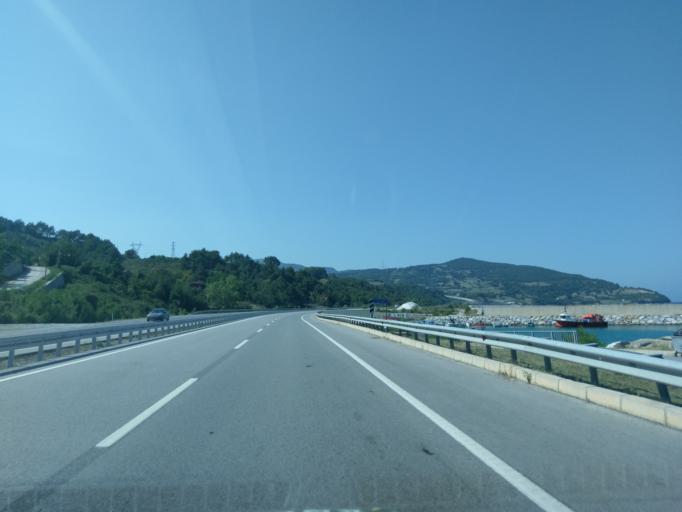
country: TR
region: Sinop
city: Dikmen
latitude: 41.7151
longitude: 35.2782
